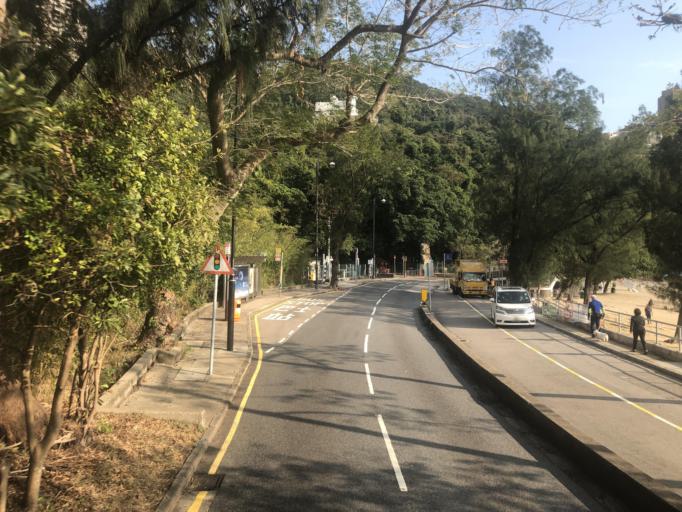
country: HK
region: Wanchai
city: Wan Chai
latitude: 22.2447
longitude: 114.1878
